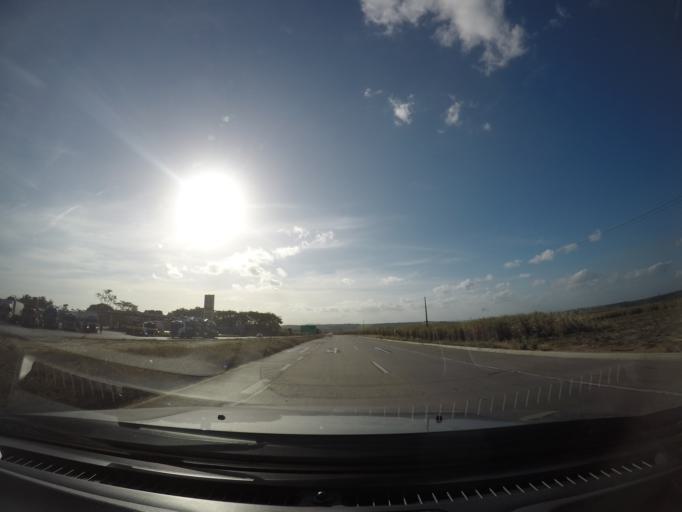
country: BR
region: Alagoas
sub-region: Pilar
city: Pilar
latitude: -9.5865
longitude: -35.9846
